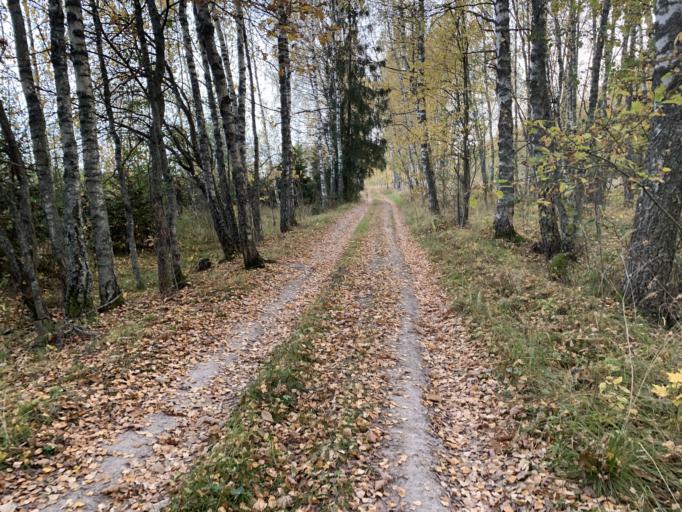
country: RU
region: Jaroslavl
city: Porech'ye-Rybnoye
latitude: 56.9856
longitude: 39.3803
